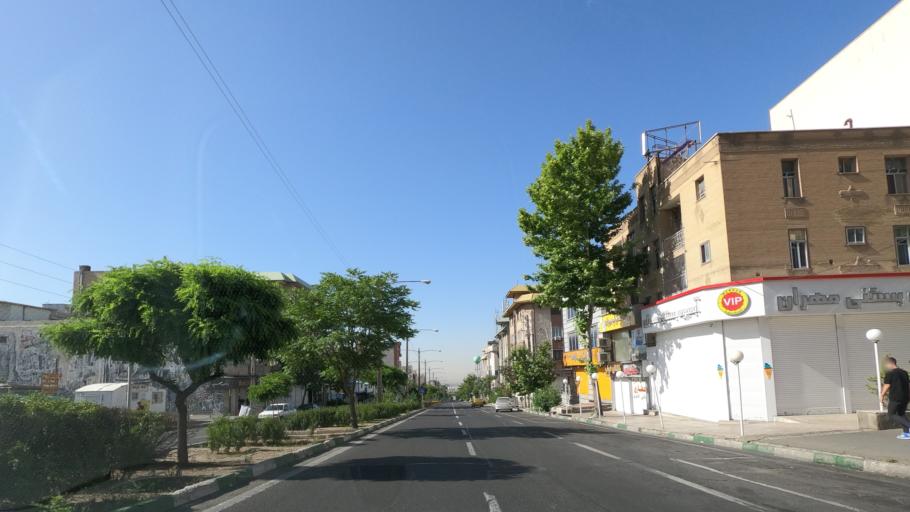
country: IR
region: Tehran
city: Tehran
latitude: 35.7535
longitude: 51.3099
